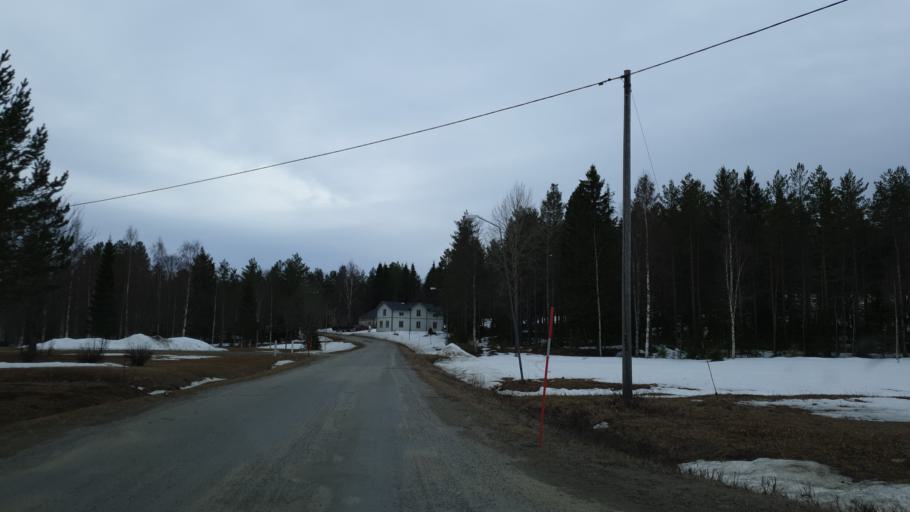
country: SE
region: Vaesterbotten
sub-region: Robertsfors Kommun
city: Robertsfors
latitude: 64.3951
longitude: 21.0016
